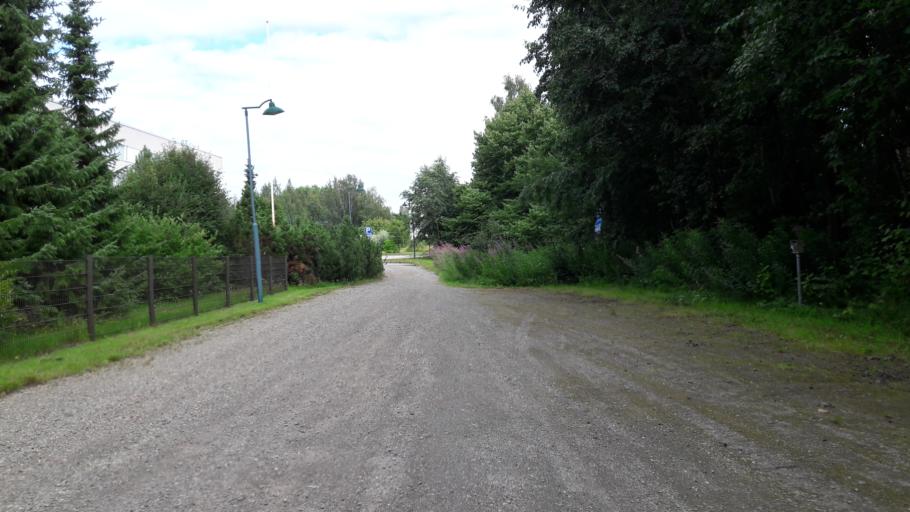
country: FI
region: North Karelia
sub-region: Joensuu
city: Joensuu
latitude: 62.5747
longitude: 29.7935
